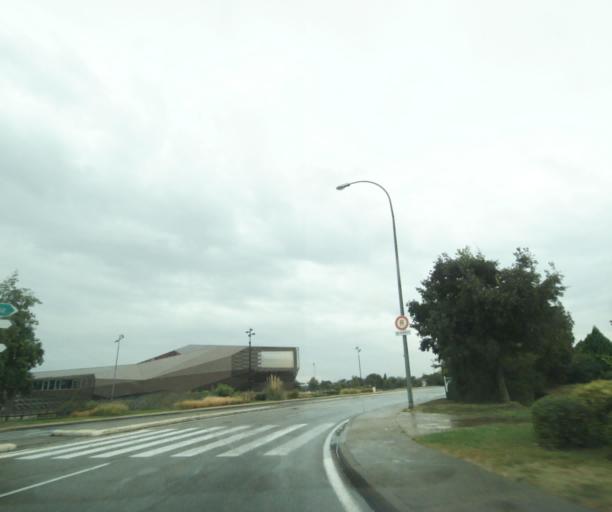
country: FR
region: Languedoc-Roussillon
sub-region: Departement du Gard
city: Rodilhan
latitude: 43.8570
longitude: 4.4045
